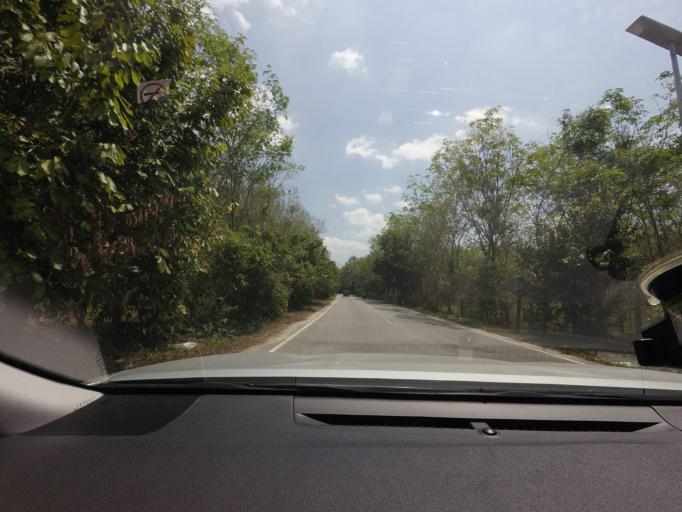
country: TH
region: Narathiwat
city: Rueso
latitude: 6.3889
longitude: 101.5037
